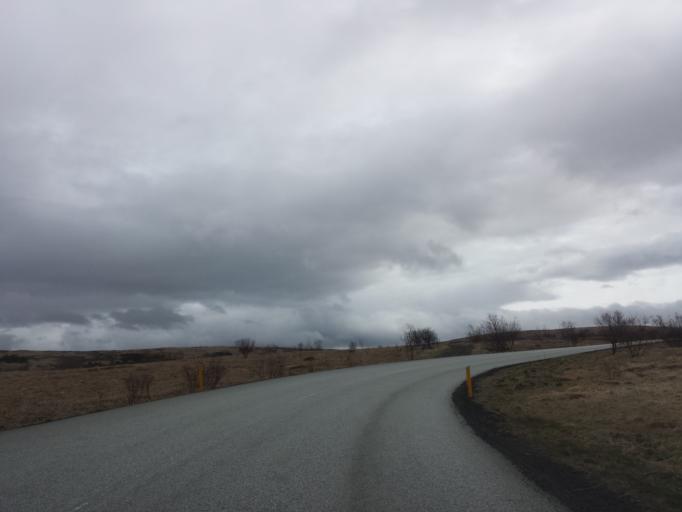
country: IS
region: Capital Region
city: Gardabaer
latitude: 64.0831
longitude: -21.8826
